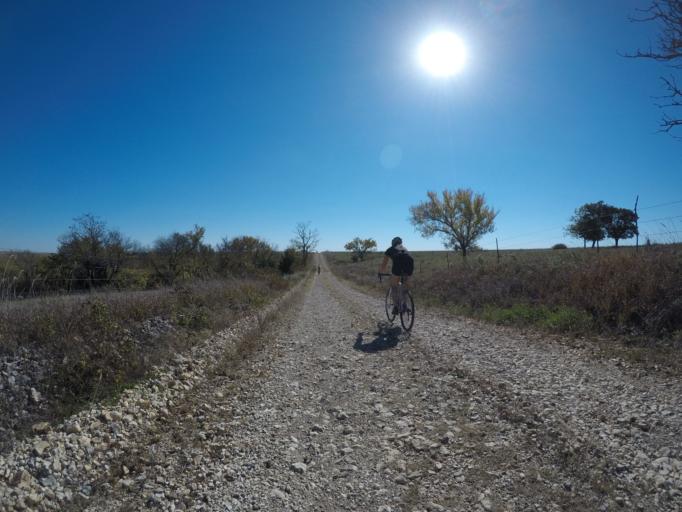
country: US
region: Kansas
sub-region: Wabaunsee County
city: Alma
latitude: 38.9748
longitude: -96.4554
